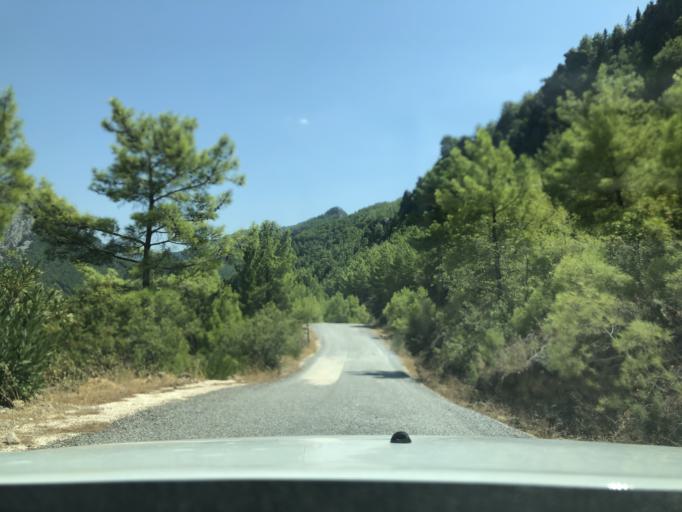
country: TR
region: Antalya
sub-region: Manavgat
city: Manavgat
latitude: 36.9093
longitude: 31.5517
